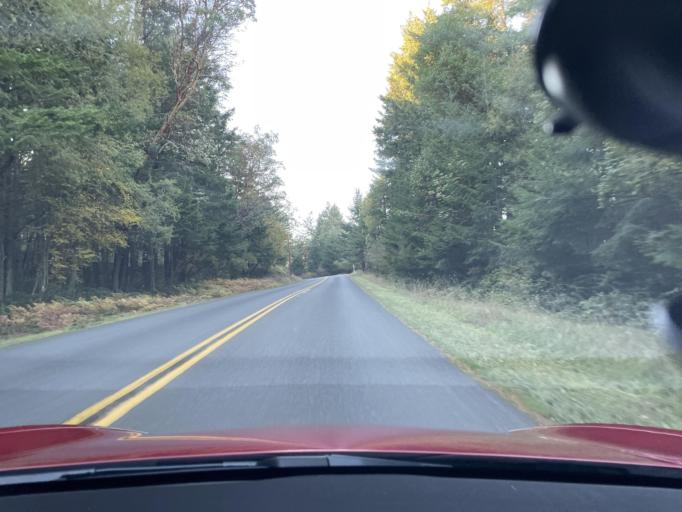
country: US
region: Washington
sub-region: San Juan County
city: Friday Harbor
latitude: 48.5571
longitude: -123.1646
